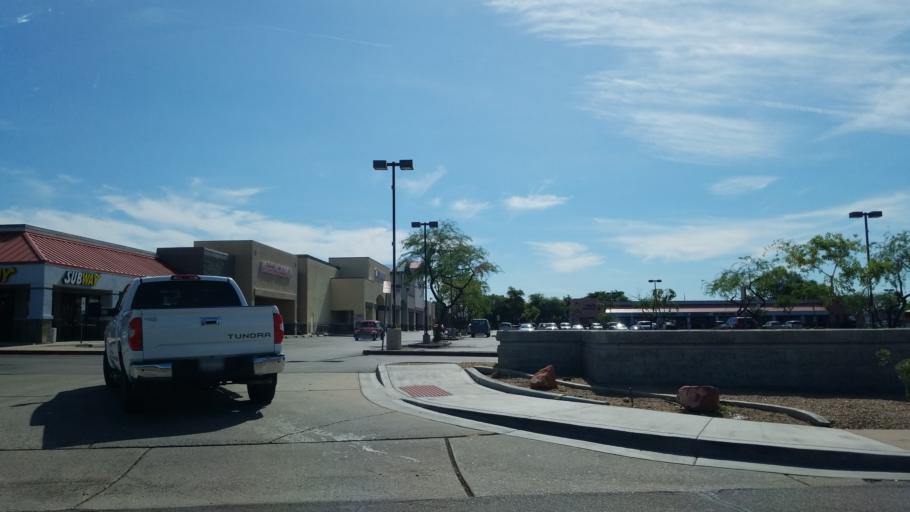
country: US
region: Arizona
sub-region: Maricopa County
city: Peoria
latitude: 33.6403
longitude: -112.1517
